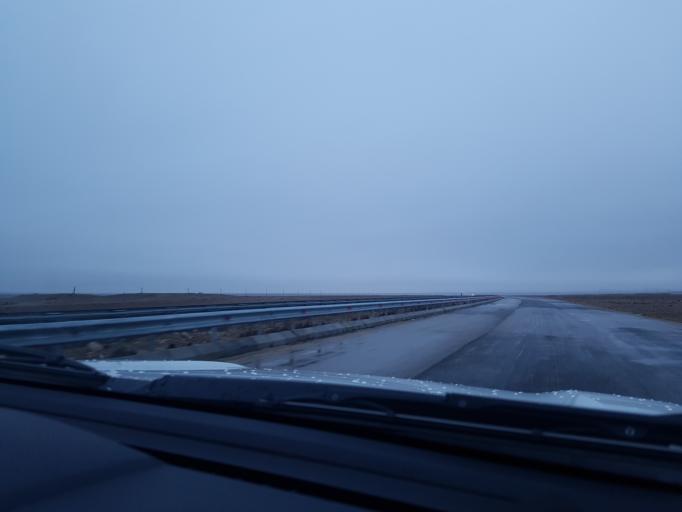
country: TM
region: Balkan
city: Balkanabat
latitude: 39.8952
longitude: 54.0152
